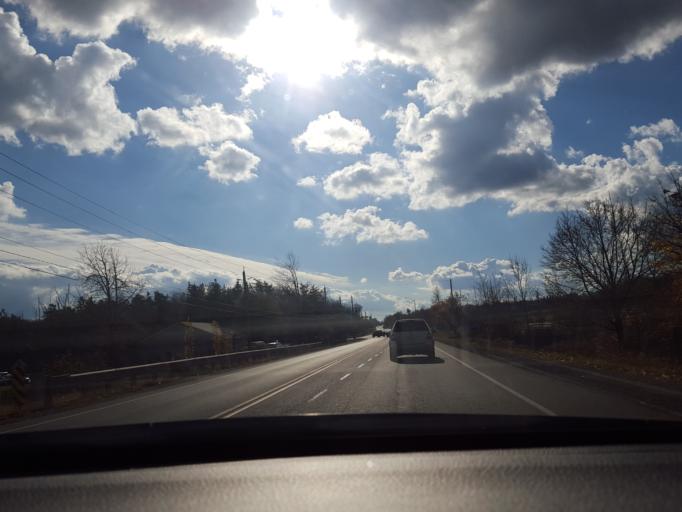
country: CA
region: Ontario
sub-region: Halton
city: Milton
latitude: 43.4686
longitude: -79.9037
